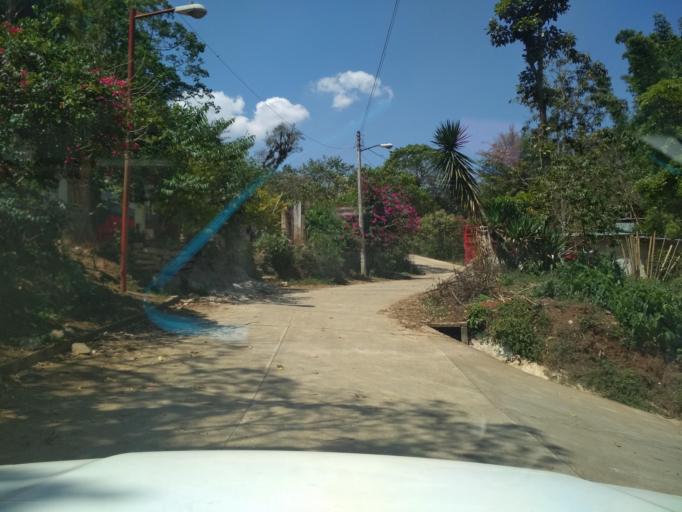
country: MX
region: Veracruz
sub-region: Tlilapan
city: Tonalixco
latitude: 18.7820
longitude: -97.0816
